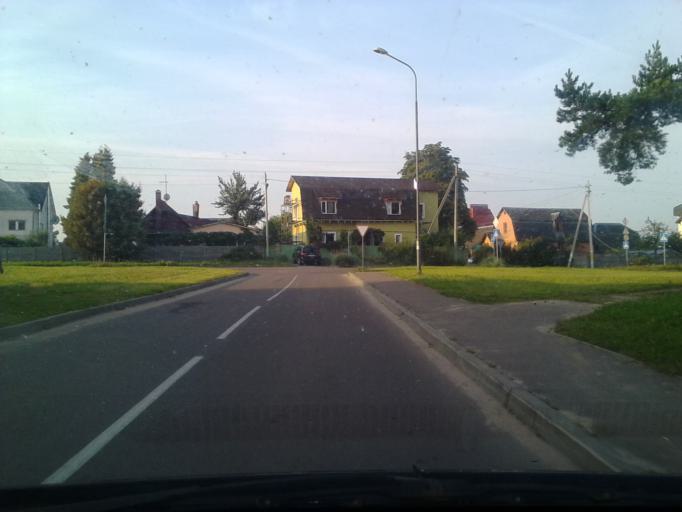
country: BY
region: Minsk
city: Minsk
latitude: 53.9481
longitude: 27.5803
